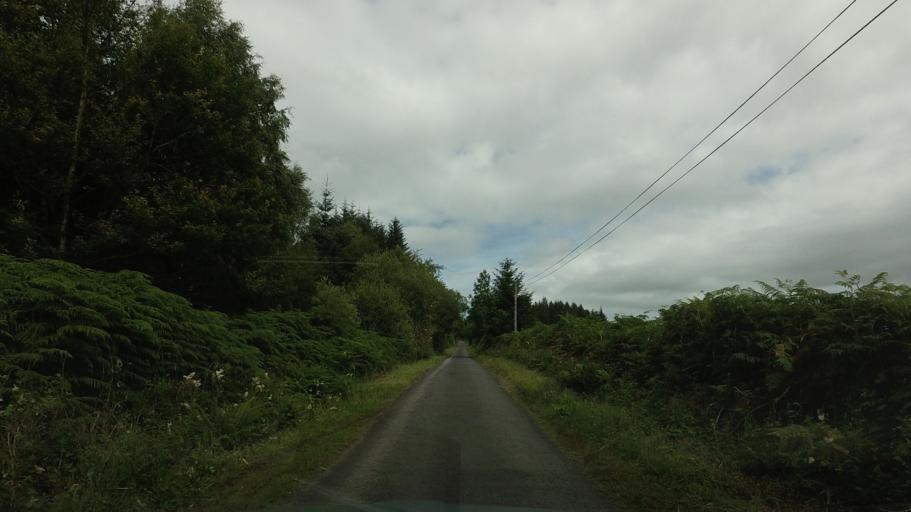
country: GB
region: Scotland
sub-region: Stirling
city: Killearn
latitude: 56.0828
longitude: -4.4475
